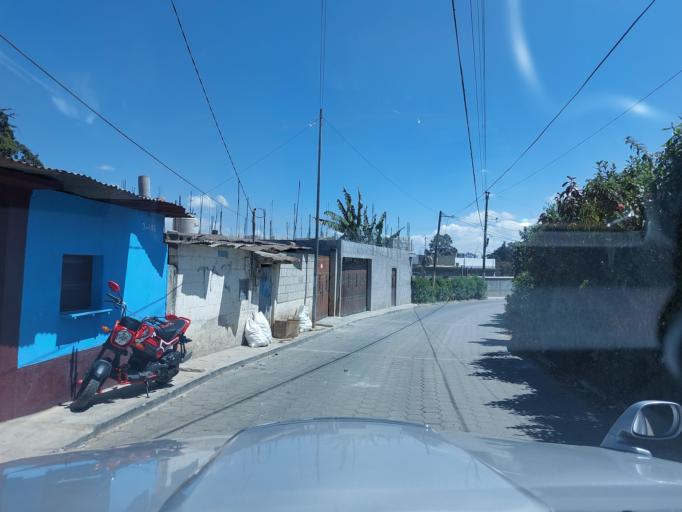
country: GT
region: Chimaltenango
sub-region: Municipio de Chimaltenango
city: Chimaltenango
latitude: 14.6561
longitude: -90.8303
